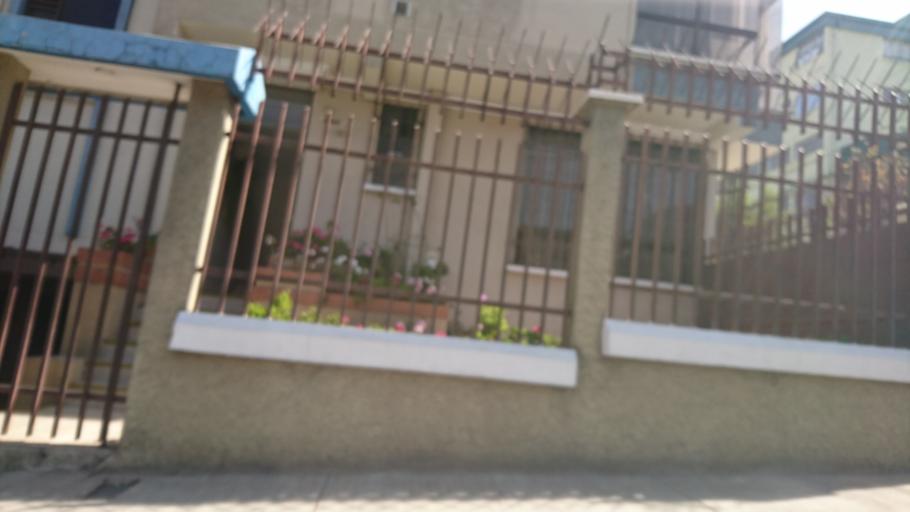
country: BO
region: La Paz
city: La Paz
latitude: -16.5000
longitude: -68.1175
